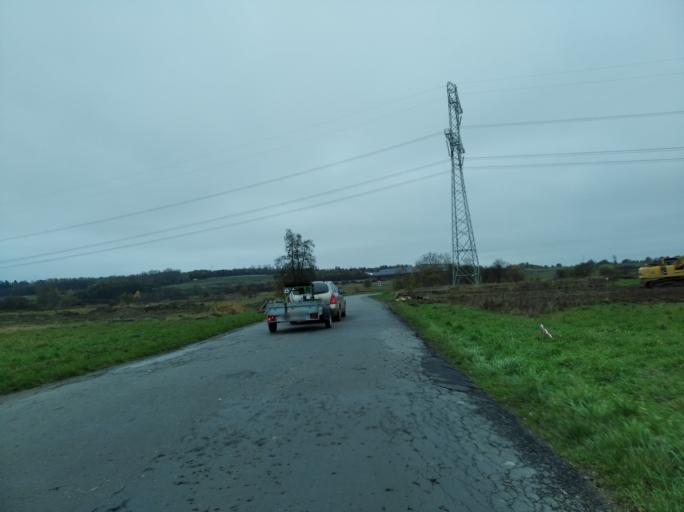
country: PL
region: Subcarpathian Voivodeship
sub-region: Powiat krosnienski
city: Odrzykon
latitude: 49.7202
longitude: 21.7618
